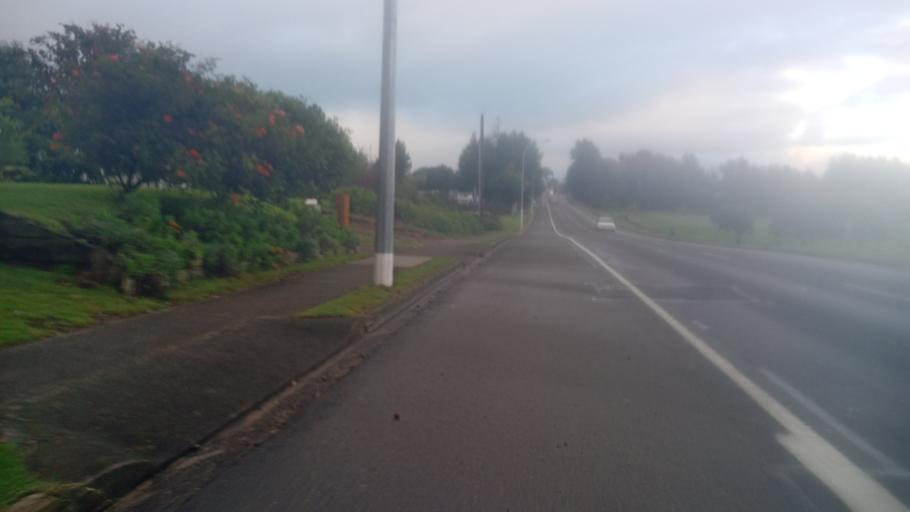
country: NZ
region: Gisborne
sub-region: Gisborne District
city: Gisborne
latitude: -38.6451
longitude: 178.0011
